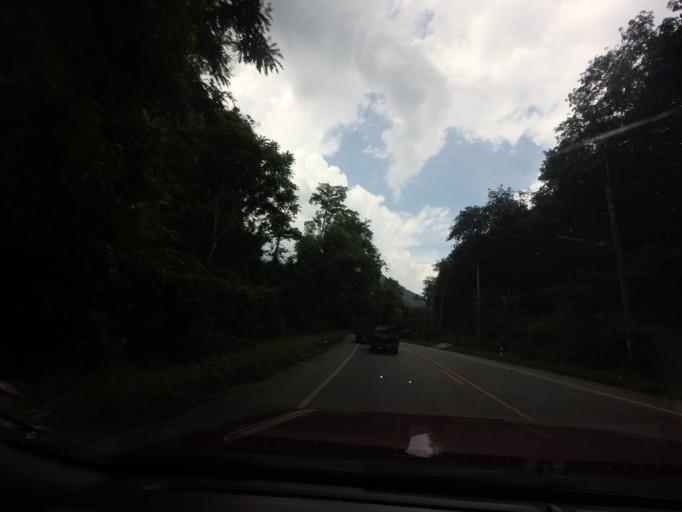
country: TH
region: Yala
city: Than To
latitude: 6.2372
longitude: 101.1757
